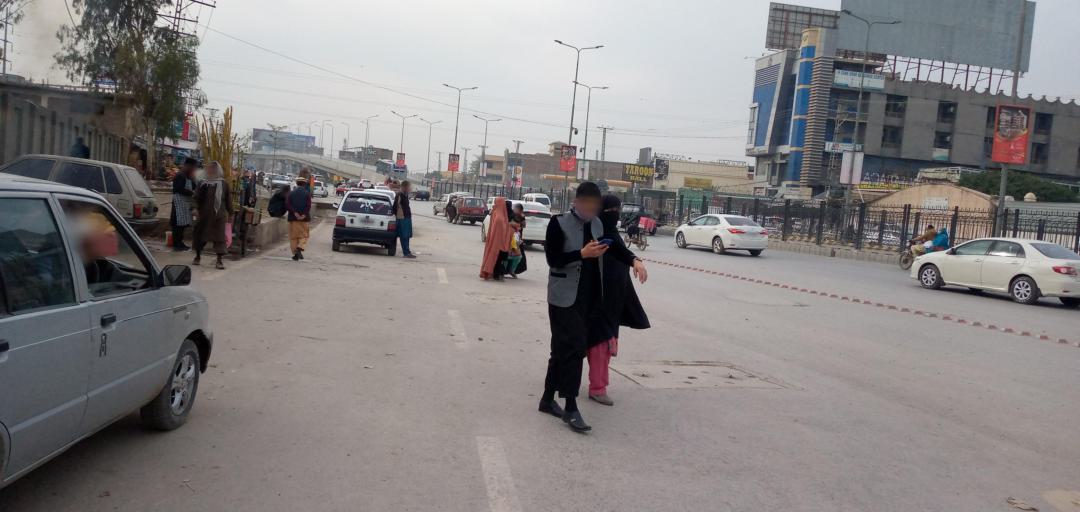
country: PK
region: Khyber Pakhtunkhwa
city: Peshawar
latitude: 33.9975
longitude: 71.4691
